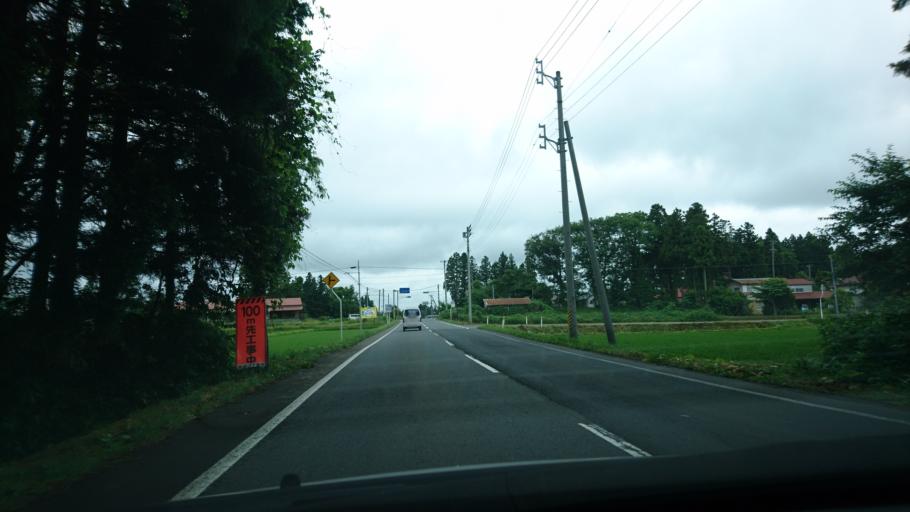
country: JP
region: Iwate
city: Mizusawa
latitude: 39.1180
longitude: 141.0528
